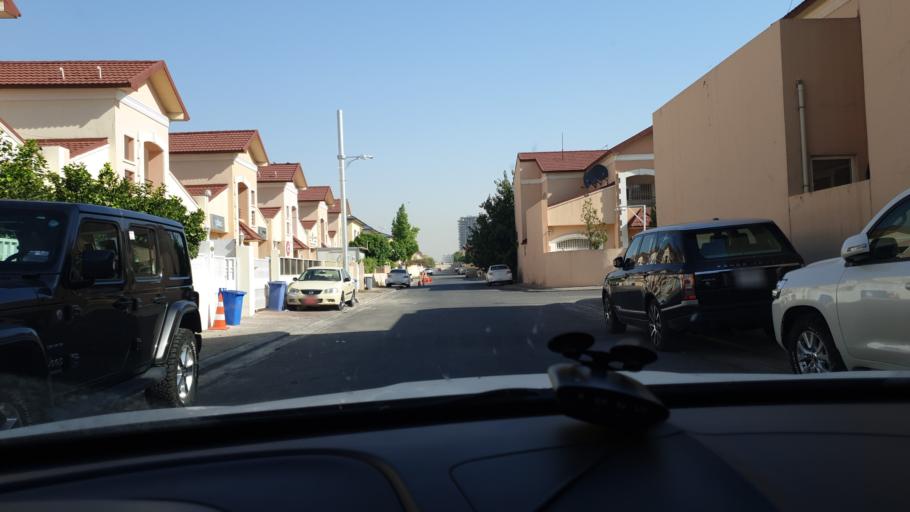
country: IQ
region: Arbil
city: Erbil
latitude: 36.1859
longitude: 43.9654
